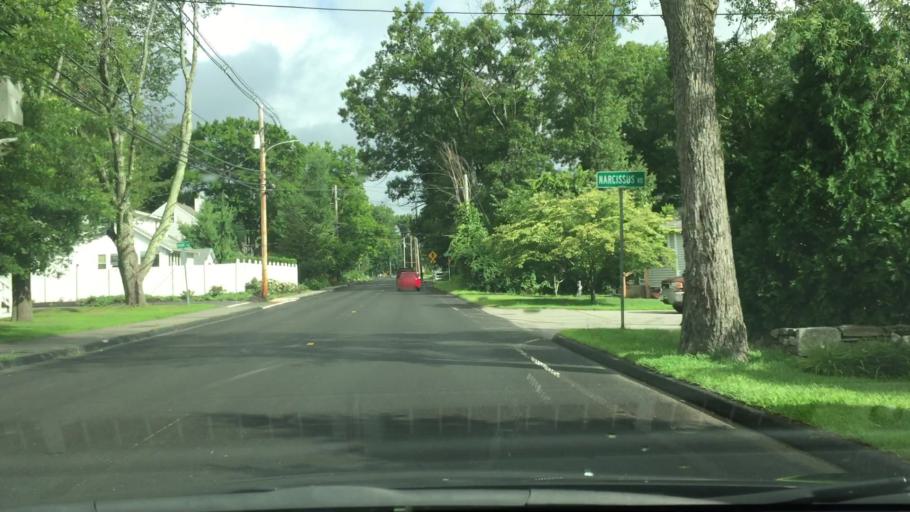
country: US
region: Massachusetts
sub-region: Middlesex County
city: Littleton Common
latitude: 42.5358
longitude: -71.4653
